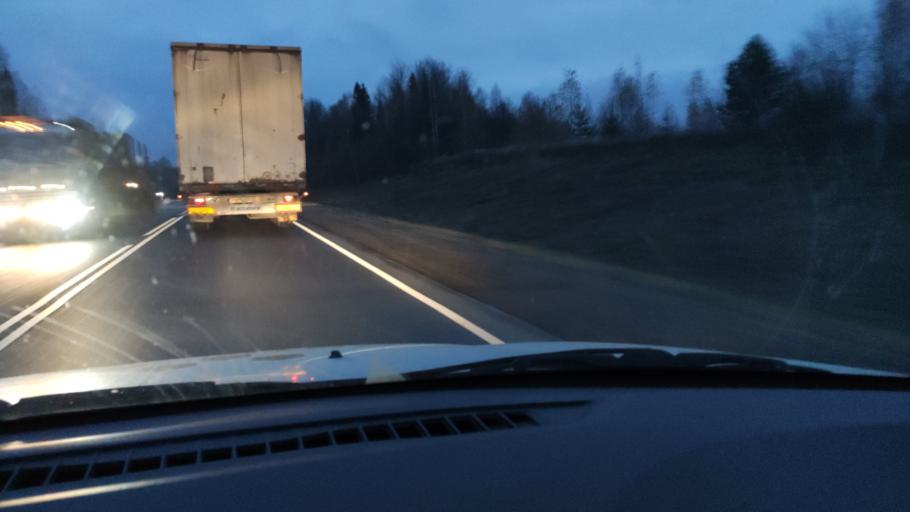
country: RU
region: Kirov
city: Kostino
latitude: 58.8337
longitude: 53.4871
